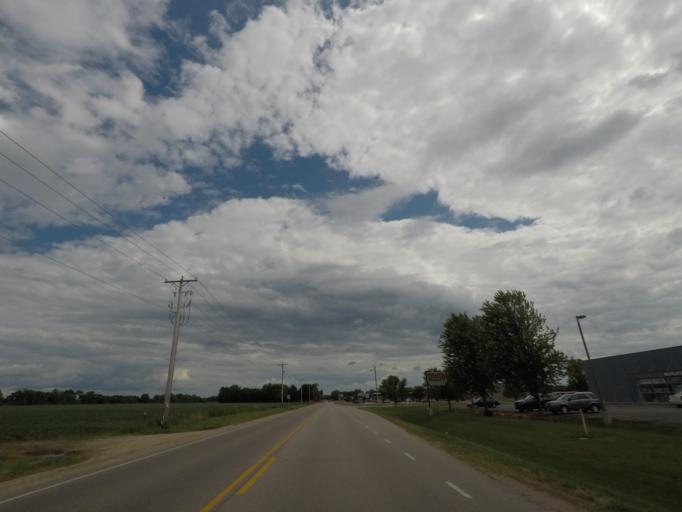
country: US
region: Wisconsin
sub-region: Dane County
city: Belleville
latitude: 42.8774
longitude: -89.5329
